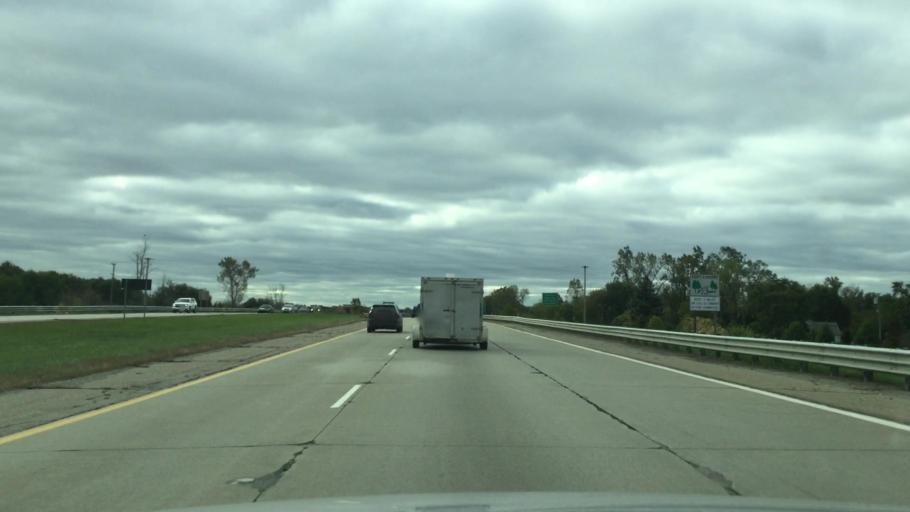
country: US
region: Michigan
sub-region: Macomb County
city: Shelby
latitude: 42.7302
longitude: -83.0269
